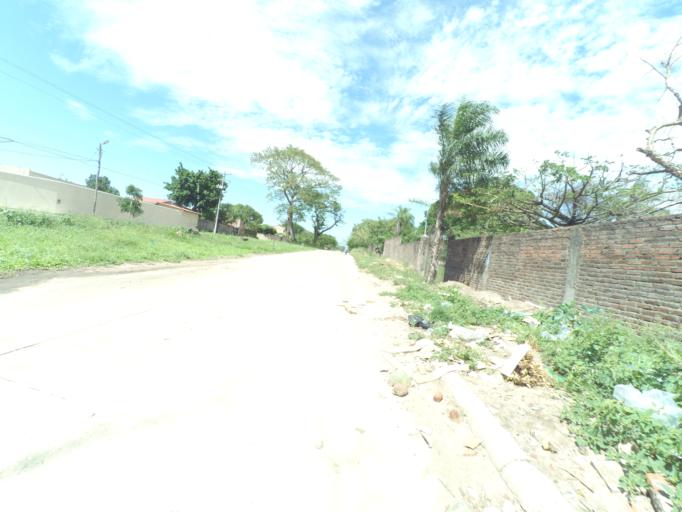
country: BO
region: Santa Cruz
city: Santa Cruz de la Sierra
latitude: -17.8082
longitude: -63.2290
